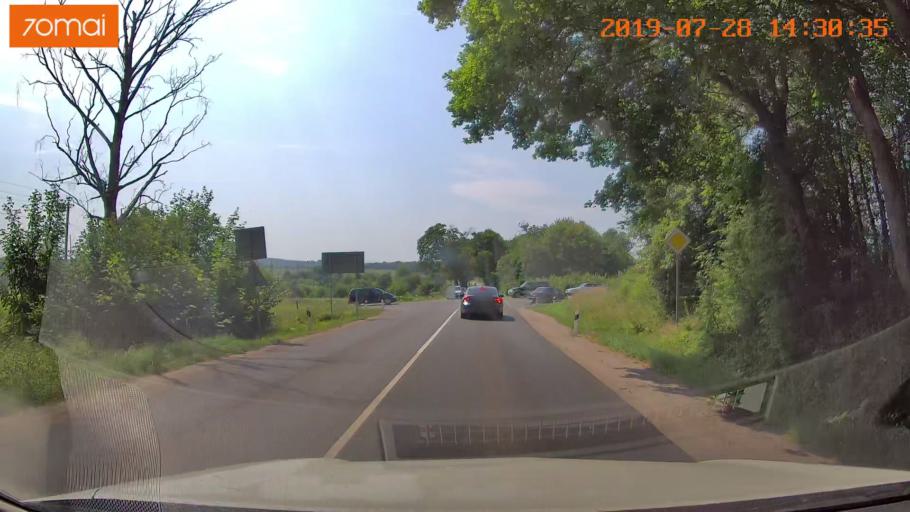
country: RU
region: Kaliningrad
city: Primorsk
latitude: 54.8027
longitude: 20.0565
